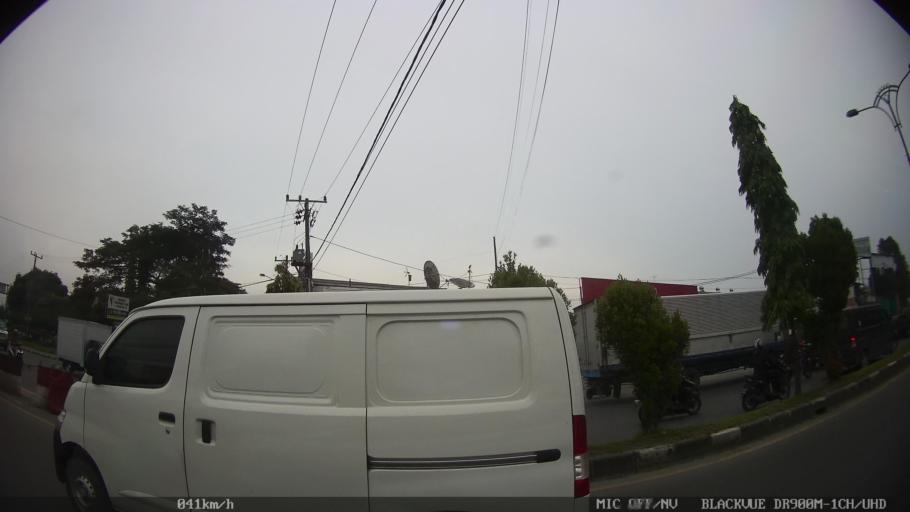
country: ID
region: North Sumatra
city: Deli Tua
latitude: 3.5327
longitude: 98.7245
